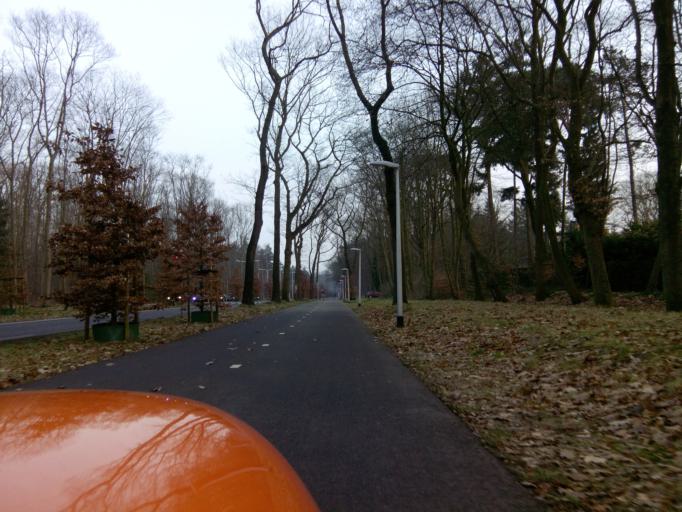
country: NL
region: Utrecht
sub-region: Gemeente Zeist
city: Zeist
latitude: 52.0994
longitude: 5.2689
